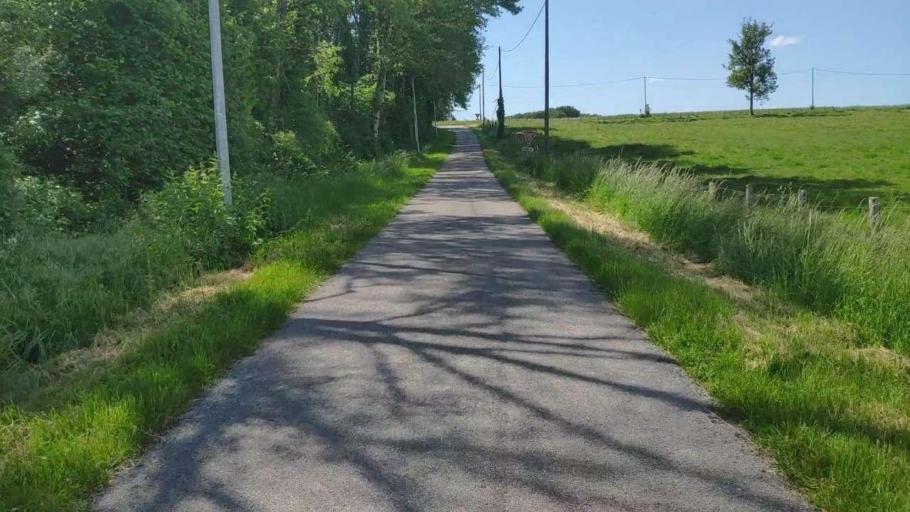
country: FR
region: Franche-Comte
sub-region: Departement du Jura
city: Bletterans
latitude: 46.8051
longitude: 5.4123
